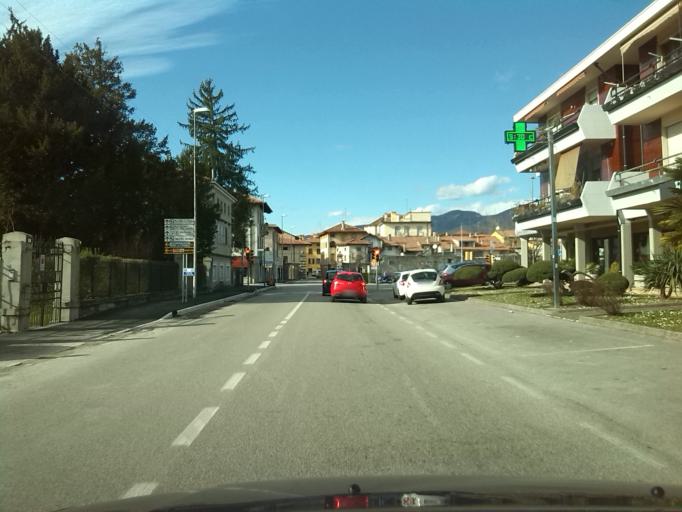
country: IT
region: Friuli Venezia Giulia
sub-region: Provincia di Udine
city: Cividale del Friuli
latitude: 46.0890
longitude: 13.4338
